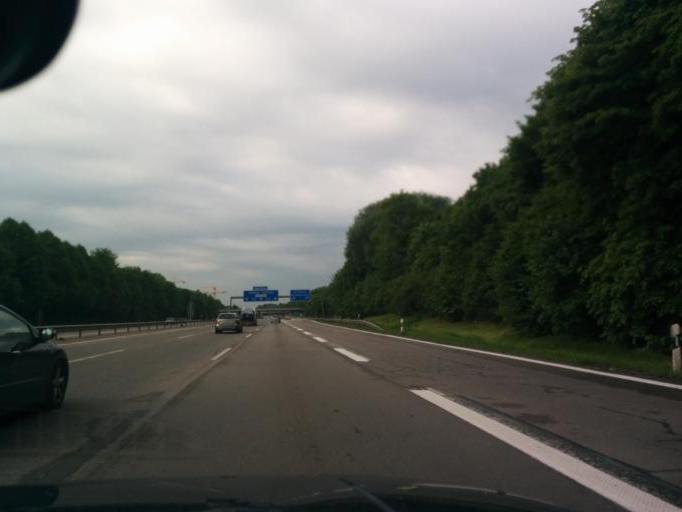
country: DE
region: Bavaria
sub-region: Upper Bavaria
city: Bogenhausen
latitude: 48.1100
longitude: 11.6149
